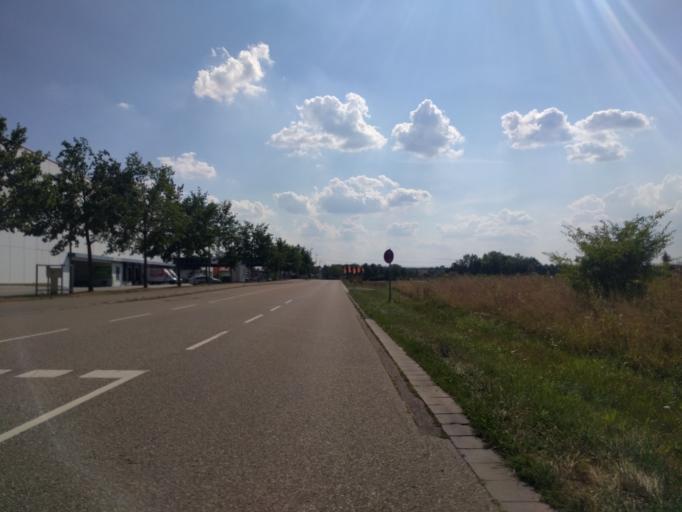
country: DE
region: Bavaria
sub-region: Upper Palatinate
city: Tegernheim
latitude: 49.0052
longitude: 12.1766
